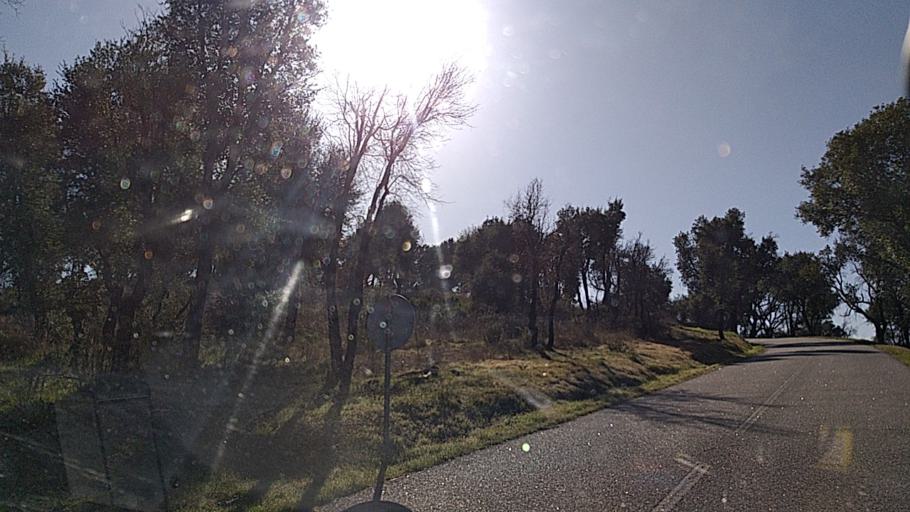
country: PT
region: Guarda
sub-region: Celorico da Beira
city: Celorico da Beira
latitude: 40.6947
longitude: -7.4497
